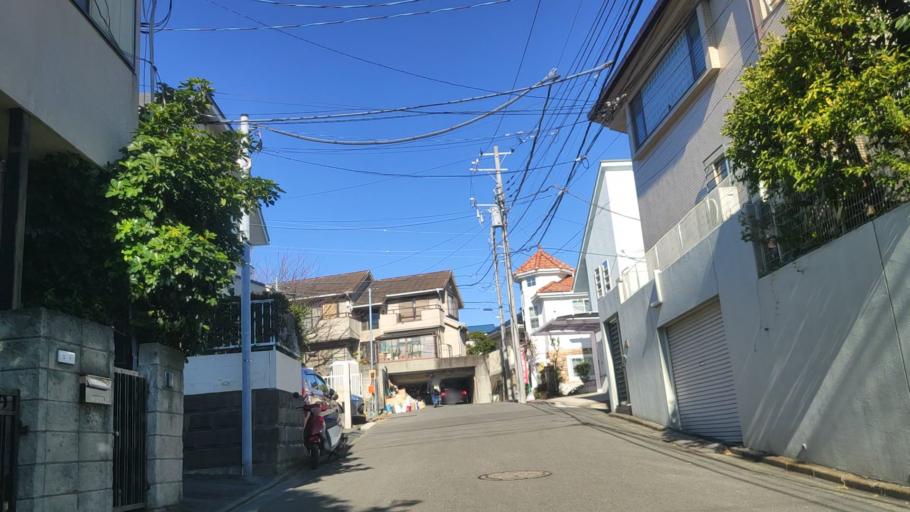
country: JP
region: Kanagawa
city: Yokohama
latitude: 35.4246
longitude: 139.6501
